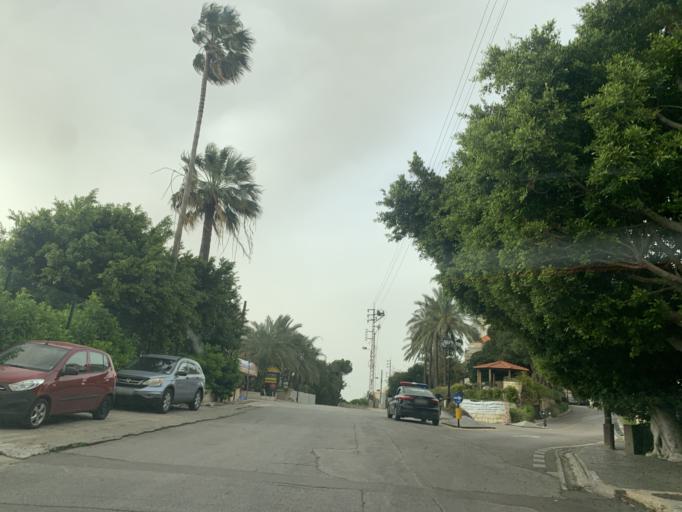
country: LB
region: Mont-Liban
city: Jbail
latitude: 34.0982
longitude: 35.6518
